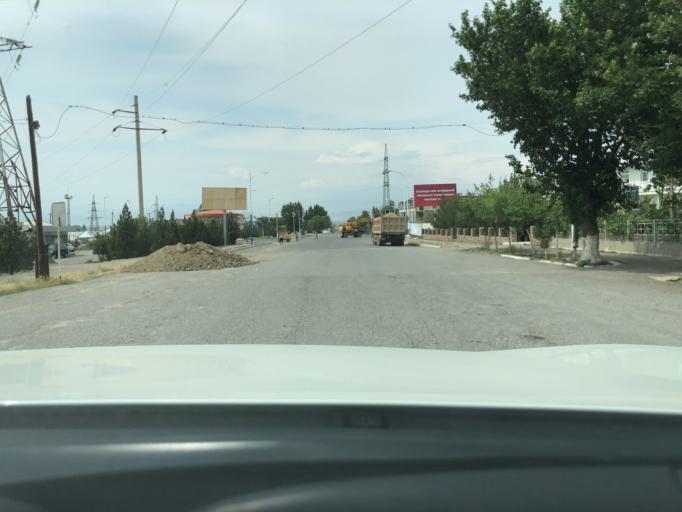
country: TJ
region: Viloyati Sughd
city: Konibodom
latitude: 40.2760
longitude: 70.4447
